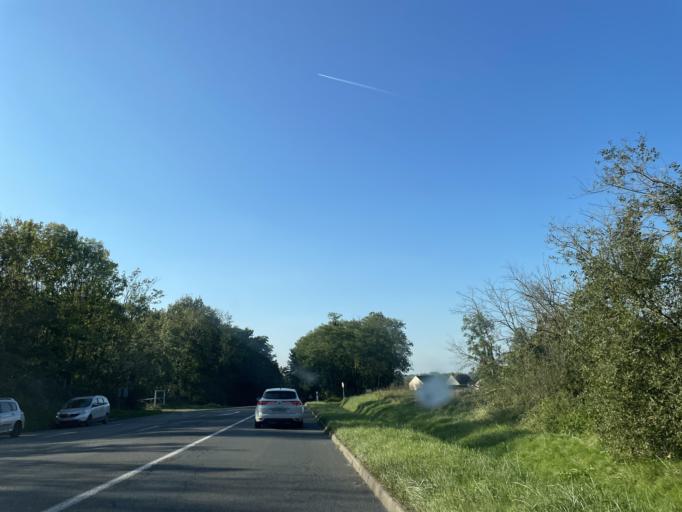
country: FR
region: Ile-de-France
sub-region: Departement de Seine-et-Marne
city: La Chapelle-sur-Crecy
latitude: 48.8495
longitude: 2.9369
